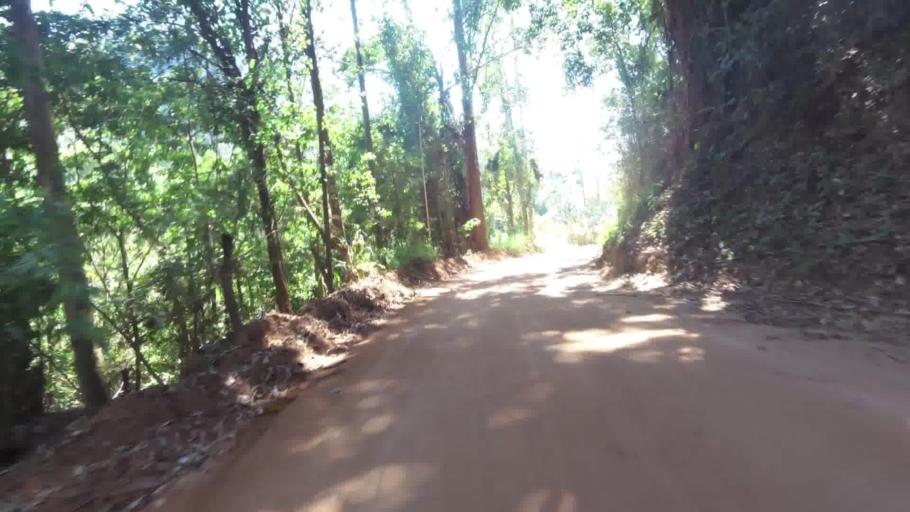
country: BR
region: Espirito Santo
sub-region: Alfredo Chaves
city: Alfredo Chaves
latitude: -20.6512
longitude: -40.8051
